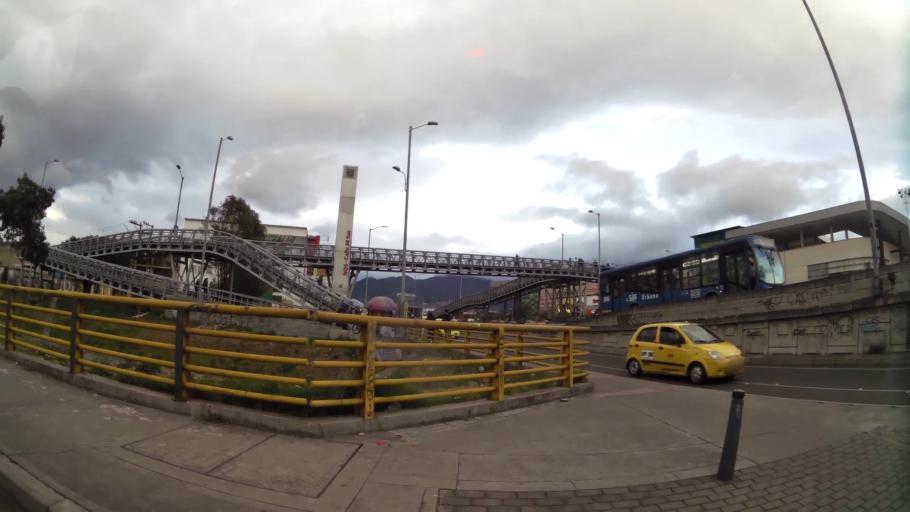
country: CO
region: Bogota D.C.
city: Bogota
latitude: 4.5939
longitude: -74.1253
